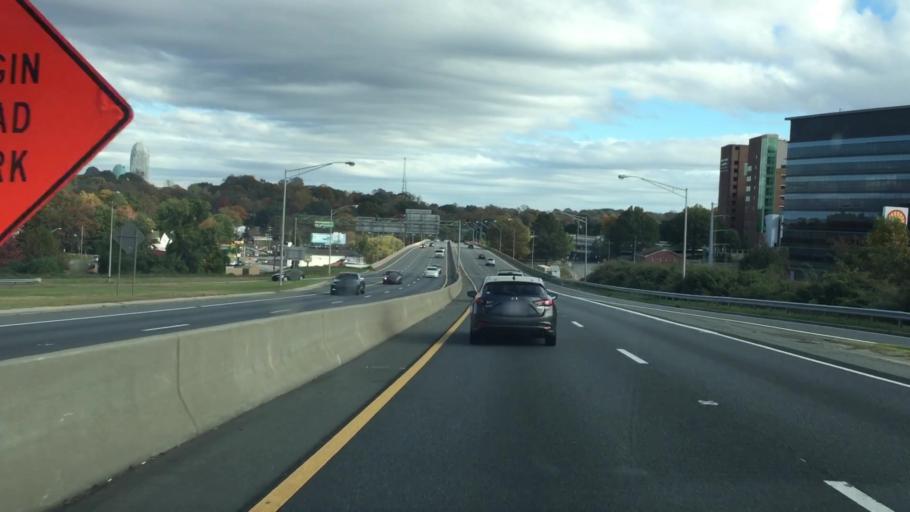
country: US
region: North Carolina
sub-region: Forsyth County
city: Winston-Salem
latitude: 36.0925
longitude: -80.2709
